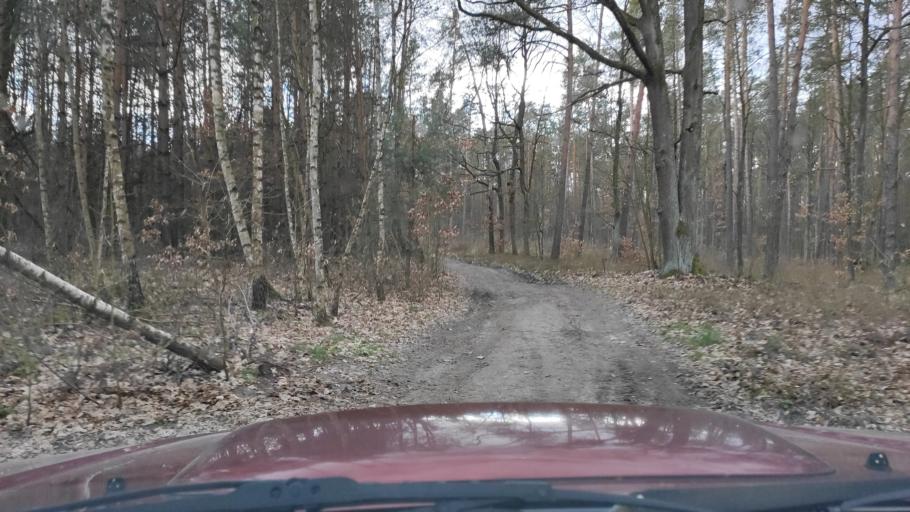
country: PL
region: Masovian Voivodeship
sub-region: Powiat kozienicki
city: Garbatka-Letnisko
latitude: 51.5076
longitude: 21.5598
